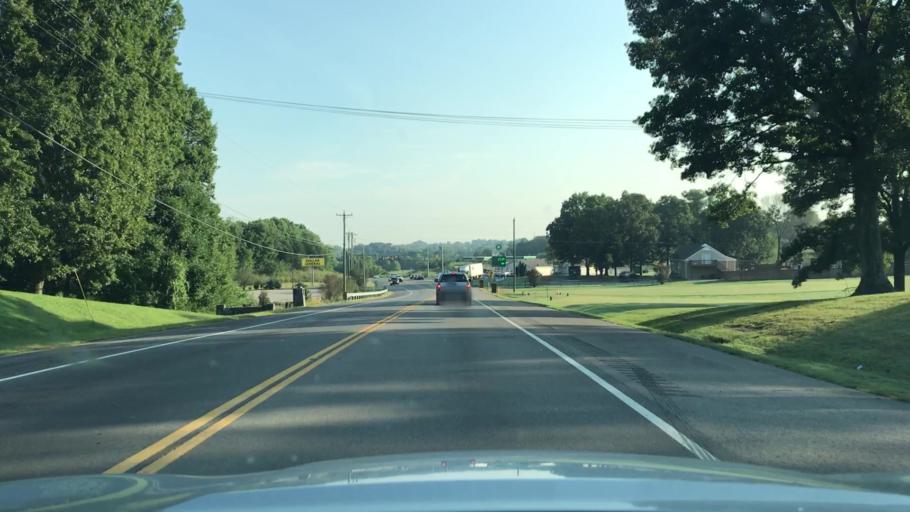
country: US
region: Tennessee
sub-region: Wilson County
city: Rural Hill
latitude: 36.1233
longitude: -86.5192
